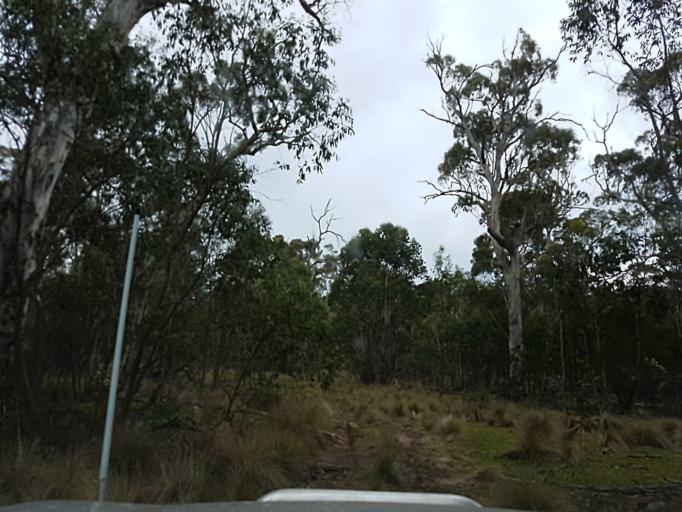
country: AU
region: New South Wales
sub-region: Snowy River
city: Jindabyne
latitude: -36.8534
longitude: 148.3347
